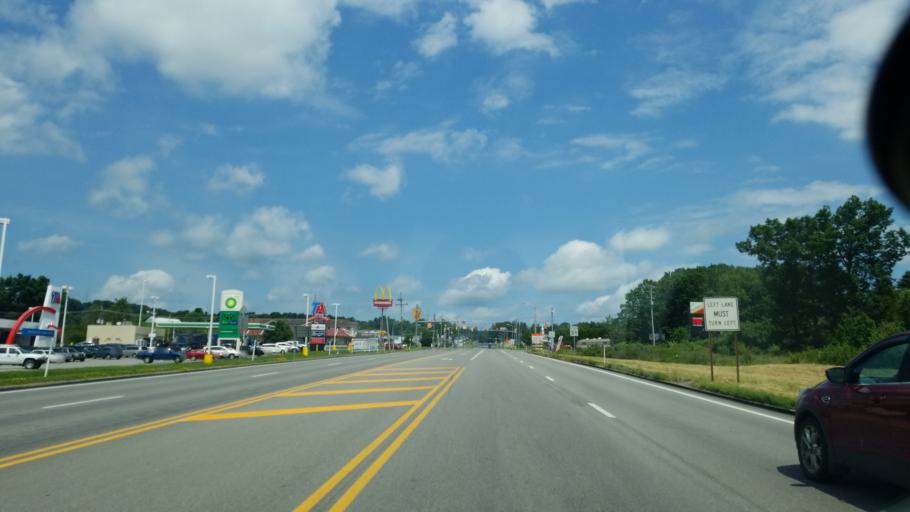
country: US
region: Pennsylvania
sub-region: Jefferson County
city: Brookville
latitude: 41.1720
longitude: -79.0980
